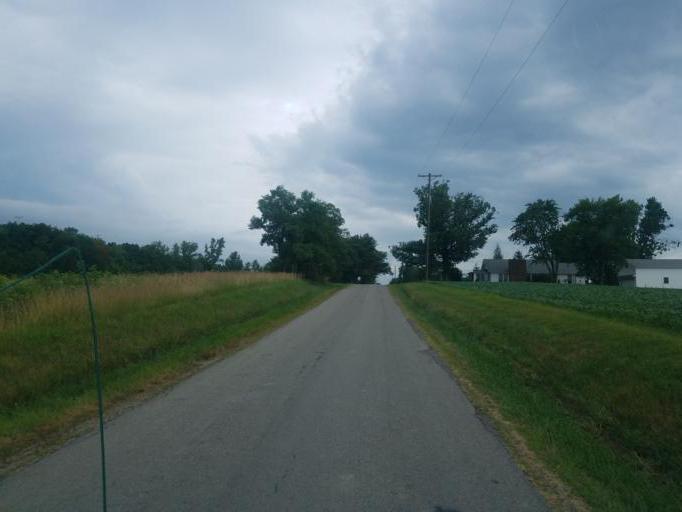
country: US
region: Ohio
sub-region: Defiance County
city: Hicksville
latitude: 41.3046
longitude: -84.8038
